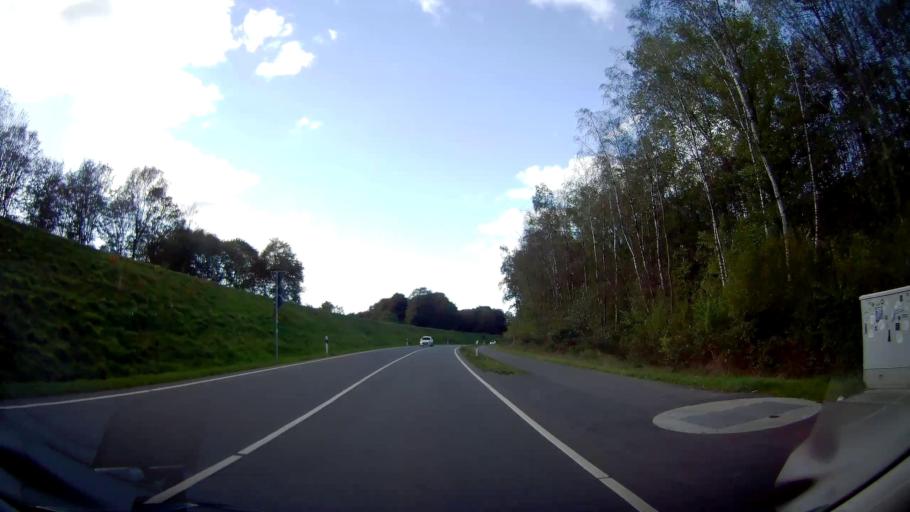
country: DE
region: North Rhine-Westphalia
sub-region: Regierungsbezirk Dusseldorf
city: Dinslaken
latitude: 51.5828
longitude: 6.7746
